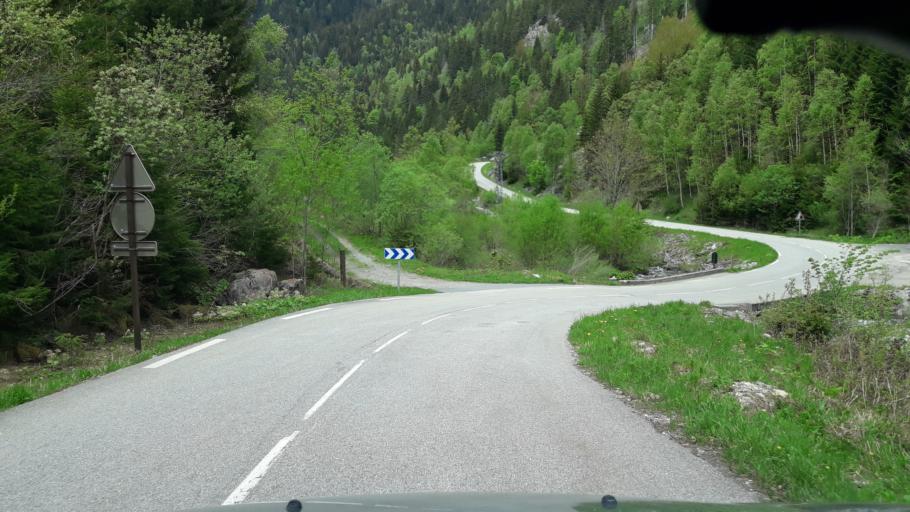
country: FR
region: Rhone-Alpes
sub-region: Departement de l'Isere
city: Theys
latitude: 45.2087
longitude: 6.0580
